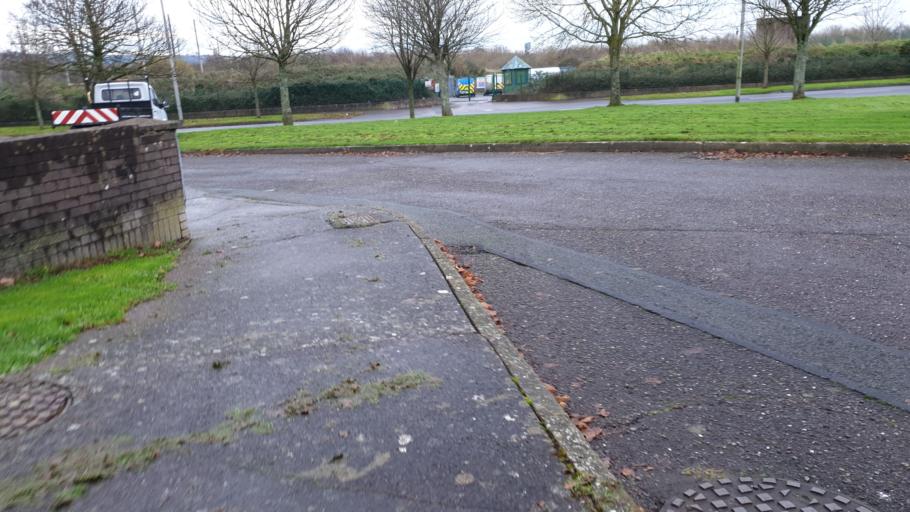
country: IE
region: Munster
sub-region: County Cork
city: Passage West
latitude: 51.8927
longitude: -8.3964
